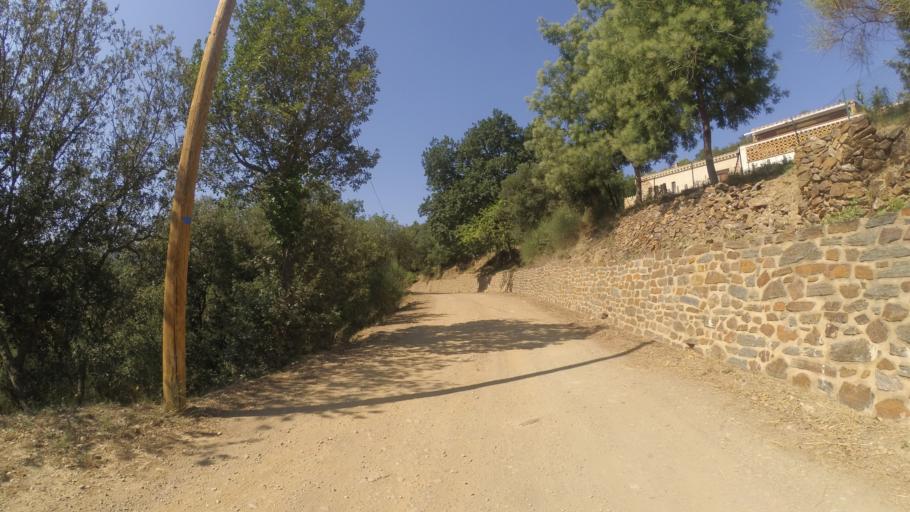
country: FR
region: Languedoc-Roussillon
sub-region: Departement des Pyrenees-Orientales
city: Millas
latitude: 42.6195
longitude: 2.6777
